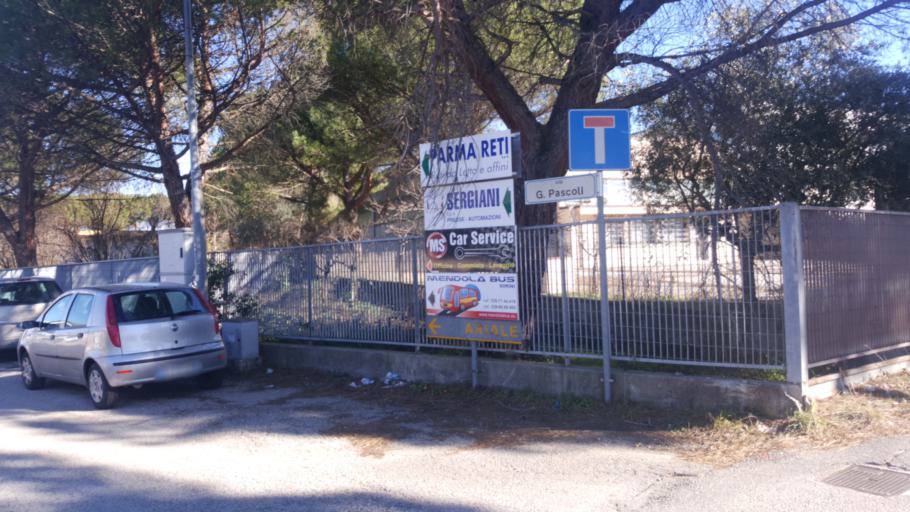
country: IT
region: Emilia-Romagna
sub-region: Provincia di Rimini
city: Cerasolo
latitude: 43.9915
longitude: 12.5373
